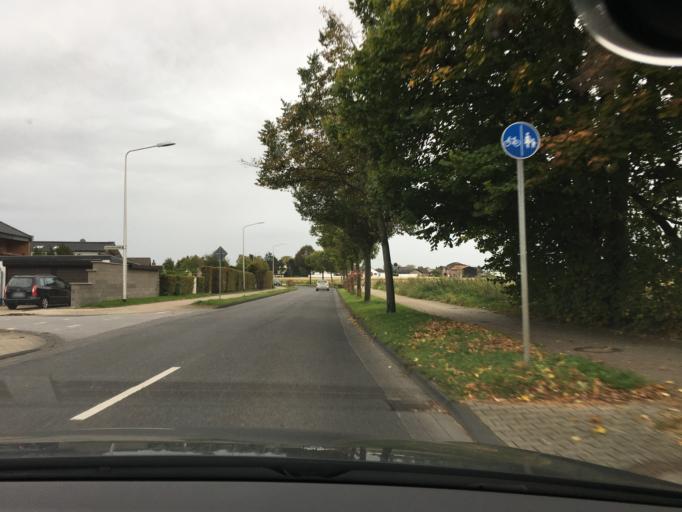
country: DE
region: North Rhine-Westphalia
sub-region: Regierungsbezirk Koln
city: Dueren
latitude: 50.7833
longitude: 6.4669
